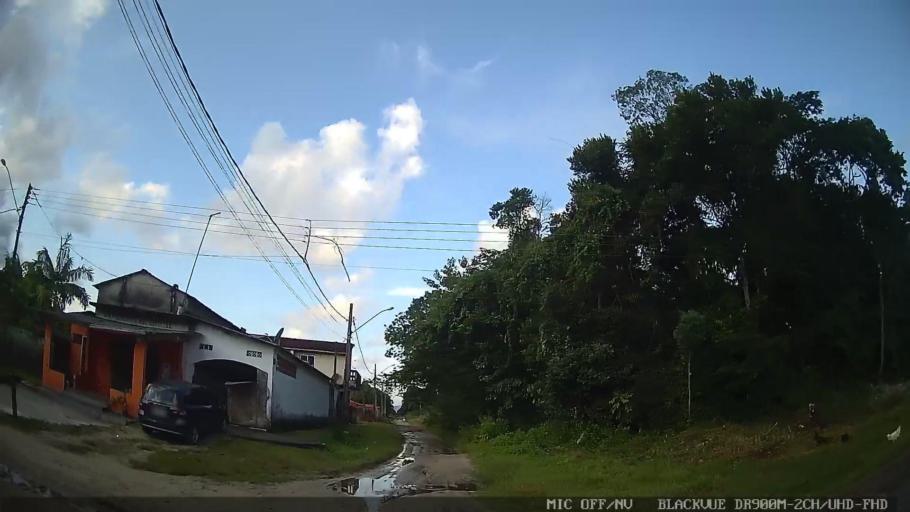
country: BR
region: Sao Paulo
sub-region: Itanhaem
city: Itanhaem
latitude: -24.1623
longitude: -46.8430
